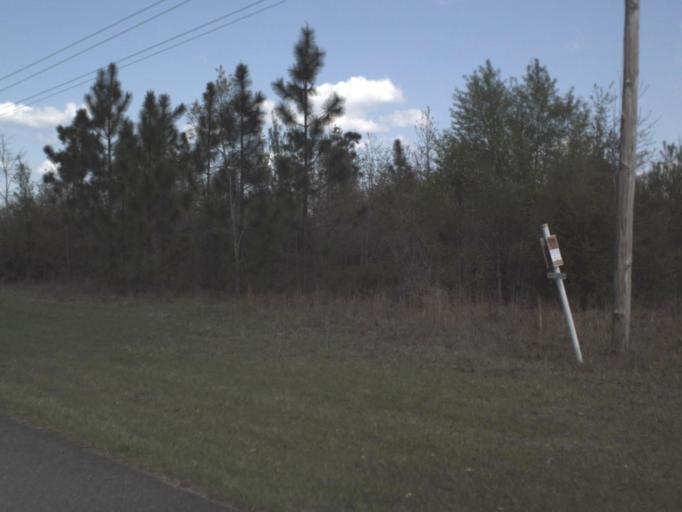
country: US
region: Alabama
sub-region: Escambia County
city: East Brewton
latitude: 30.9480
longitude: -87.0747
